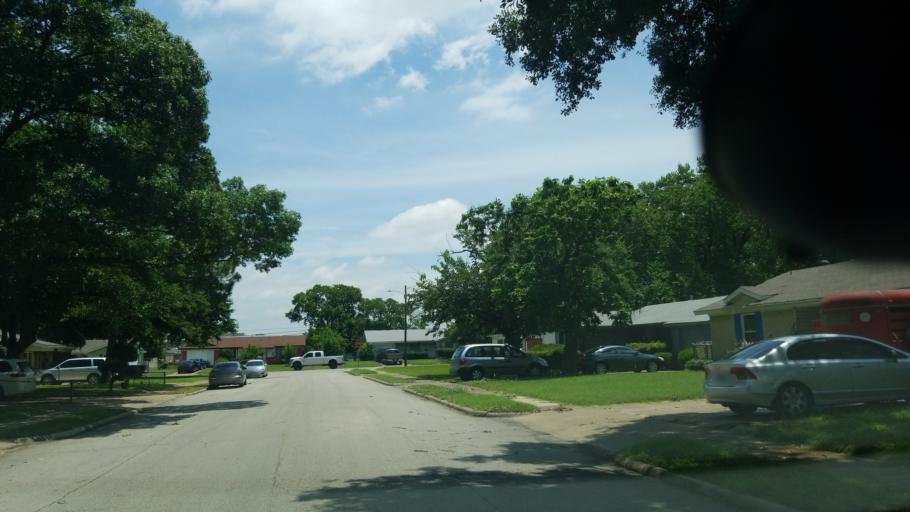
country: US
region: Texas
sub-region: Dallas County
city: Irving
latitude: 32.8497
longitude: -96.9691
